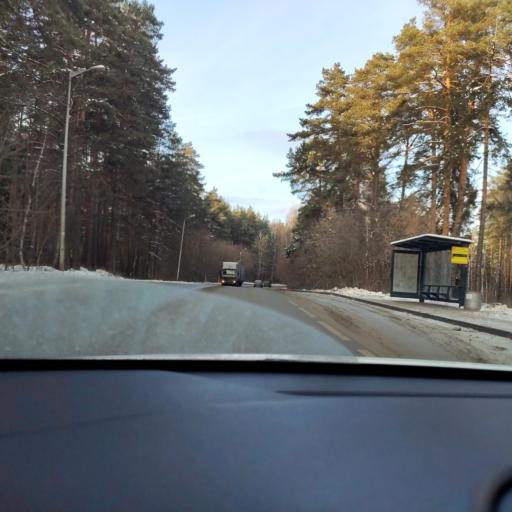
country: RU
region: Tatarstan
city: Osinovo
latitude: 55.8286
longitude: 48.8939
